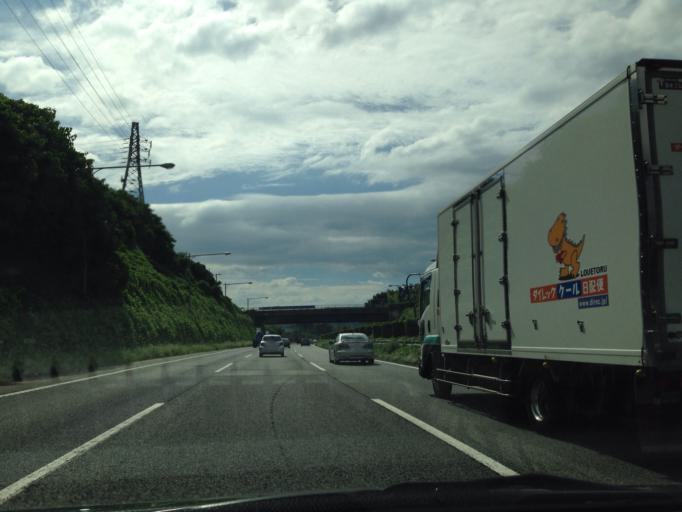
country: JP
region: Kanagawa
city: Hadano
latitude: 35.3504
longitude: 139.2275
